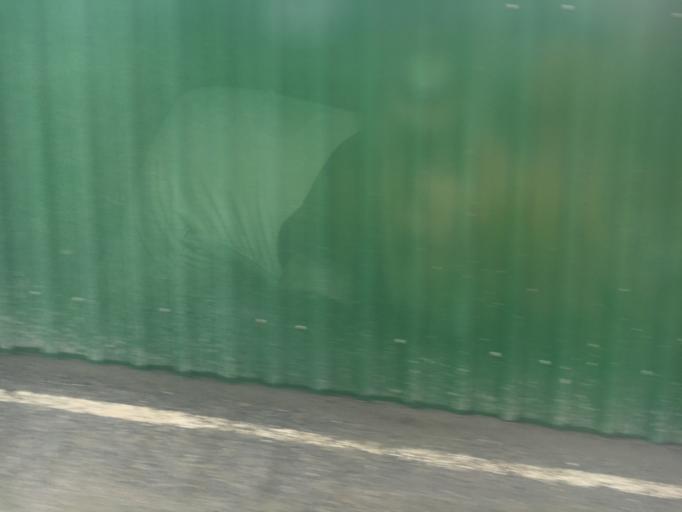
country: TR
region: Istanbul
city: UEskuedar
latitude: 41.0813
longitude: 29.0547
